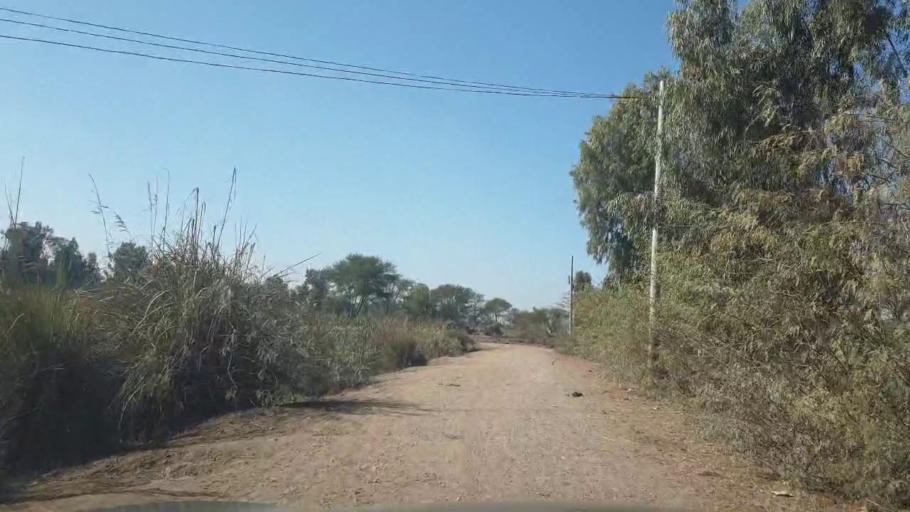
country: PK
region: Sindh
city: Mirpur Mathelo
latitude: 28.0601
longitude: 69.5114
